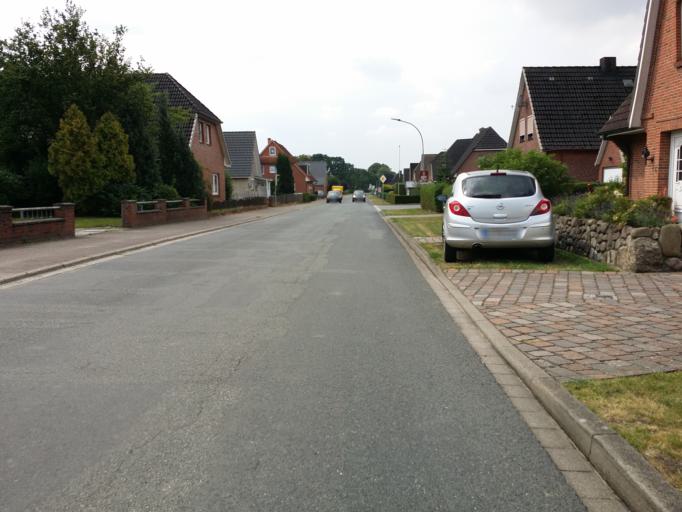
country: DE
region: Schleswig-Holstein
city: Heiligenstedtenerkamp
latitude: 53.9023
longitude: 9.4724
